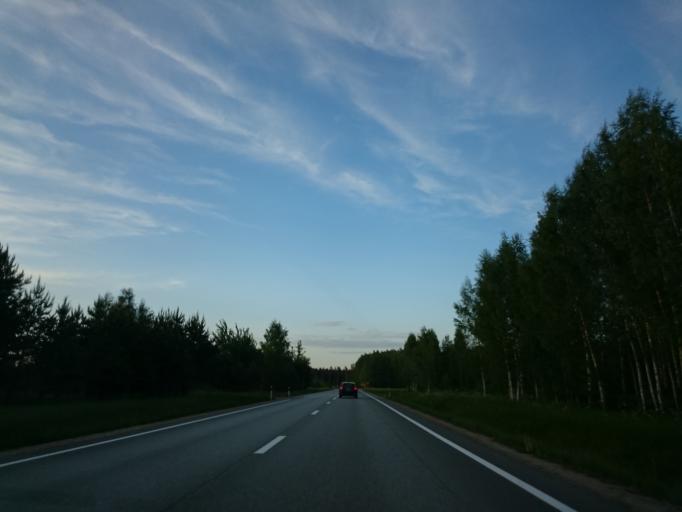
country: LV
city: Tireli
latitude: 56.8615
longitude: 23.6153
